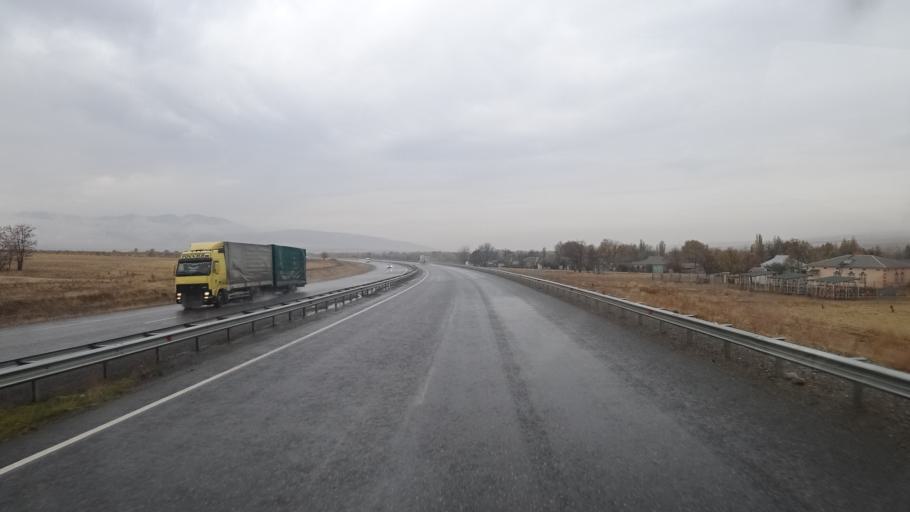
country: KZ
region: Ongtustik Qazaqstan
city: Kokterek
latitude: 42.5466
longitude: 70.2363
